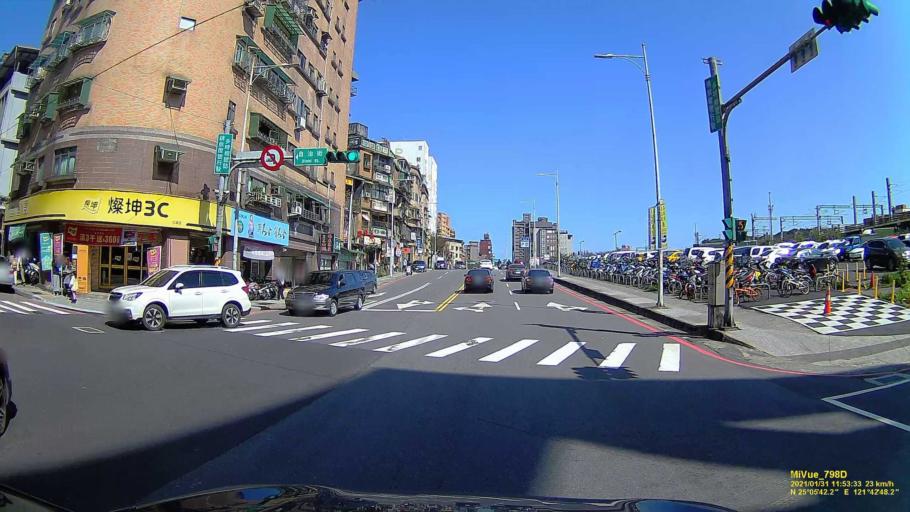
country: TW
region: Taiwan
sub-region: Keelung
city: Keelung
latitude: 25.0951
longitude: 121.7135
